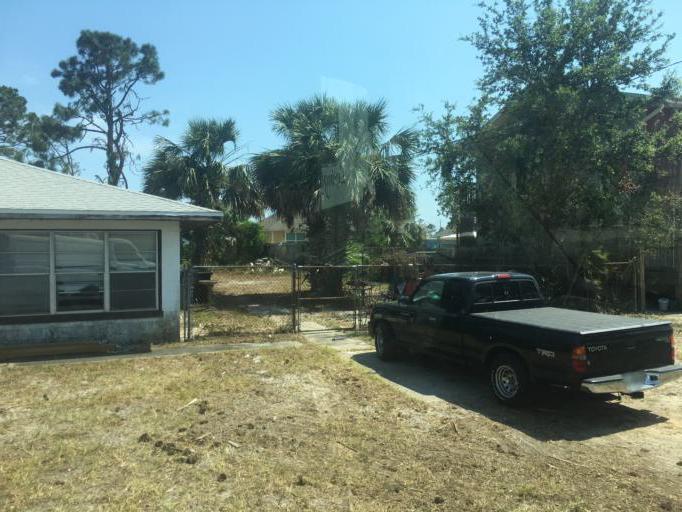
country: US
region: Florida
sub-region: Bay County
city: Lower Grand Lagoon
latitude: 30.1476
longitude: -85.7518
